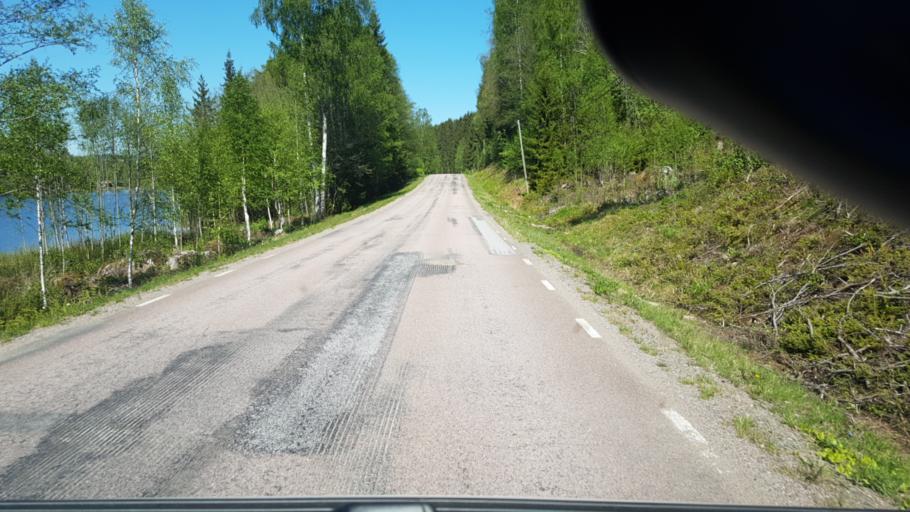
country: SE
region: Vaermland
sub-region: Eda Kommun
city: Amotfors
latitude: 59.8965
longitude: 12.5253
